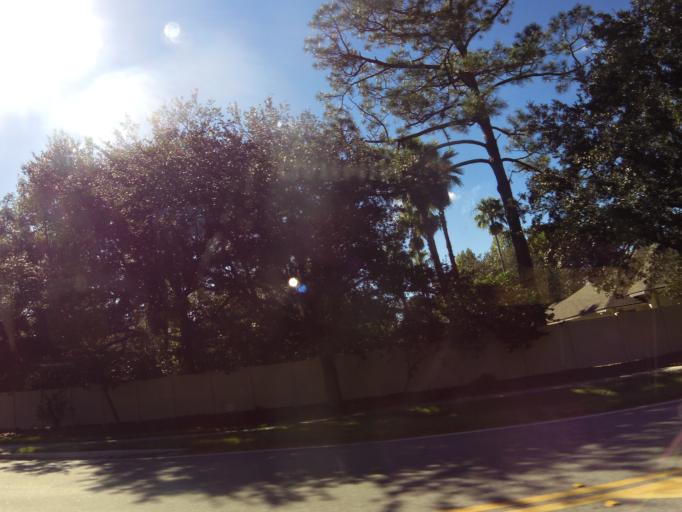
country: US
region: Florida
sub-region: Saint Johns County
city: Palm Valley
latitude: 30.1458
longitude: -81.3771
